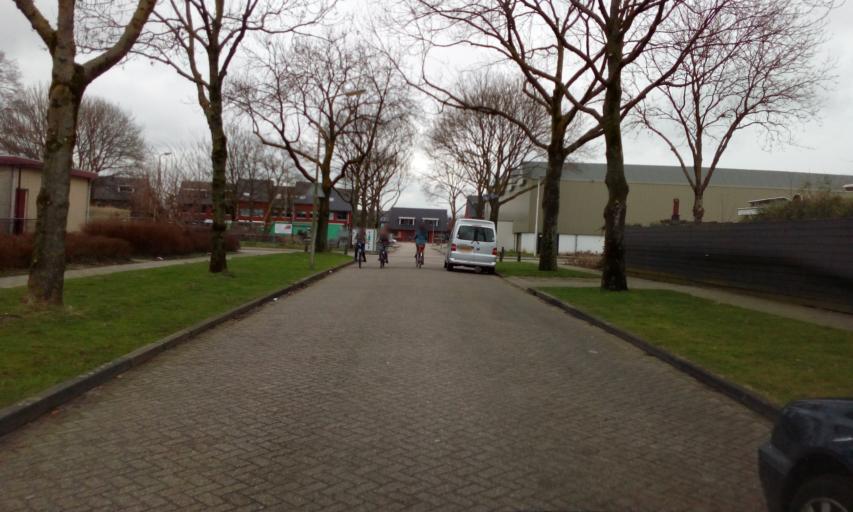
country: NL
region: South Holland
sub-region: Gemeente Alblasserdam
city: Alblasserdam
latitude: 51.8683
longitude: 4.6619
